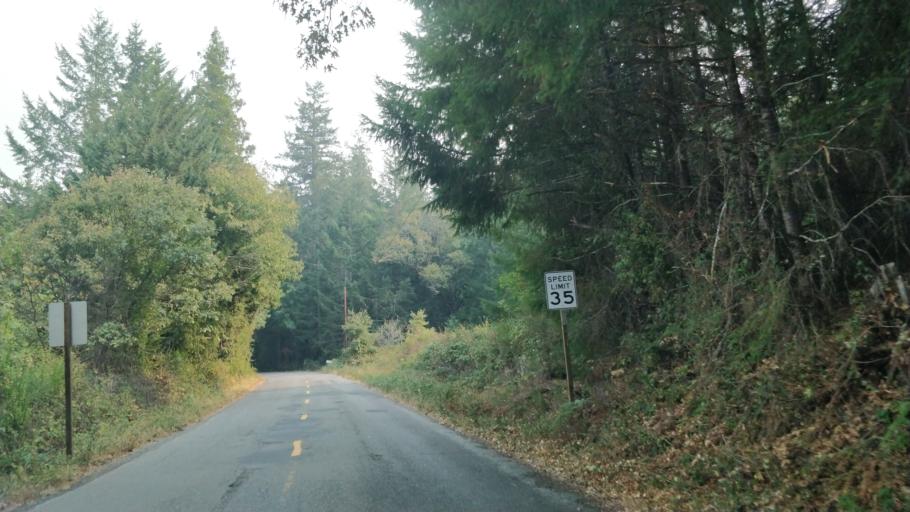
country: US
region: California
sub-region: Humboldt County
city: Rio Dell
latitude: 40.2364
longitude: -124.1590
